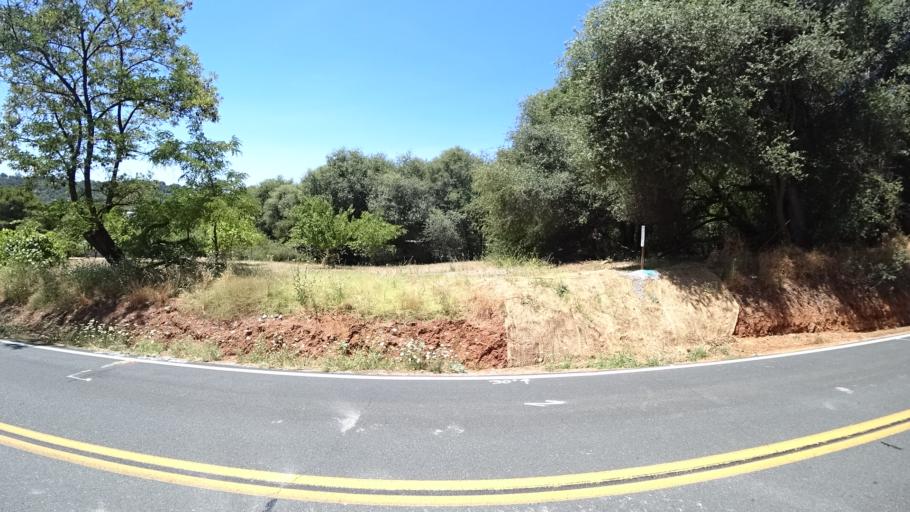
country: US
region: California
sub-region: Amador County
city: Jackson
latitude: 38.3001
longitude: -120.6977
